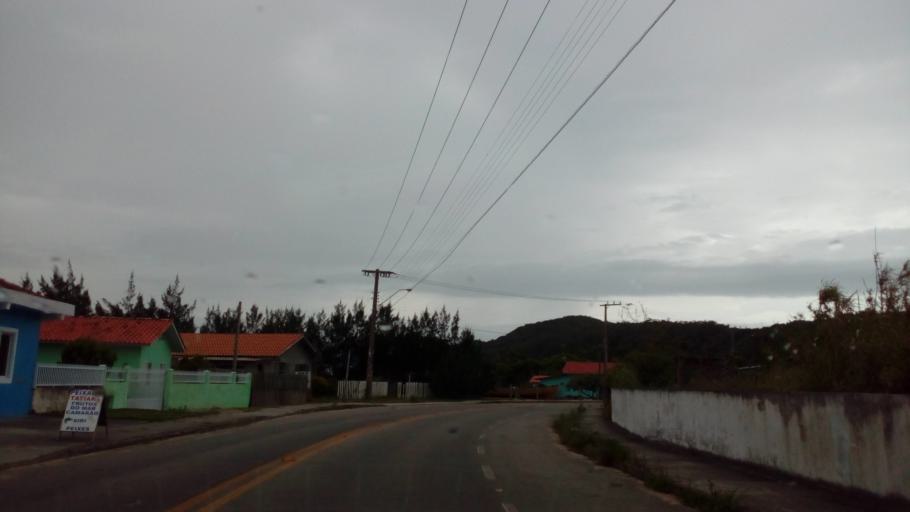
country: BR
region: Santa Catarina
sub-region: Laguna
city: Laguna
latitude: -28.5169
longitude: -48.7712
